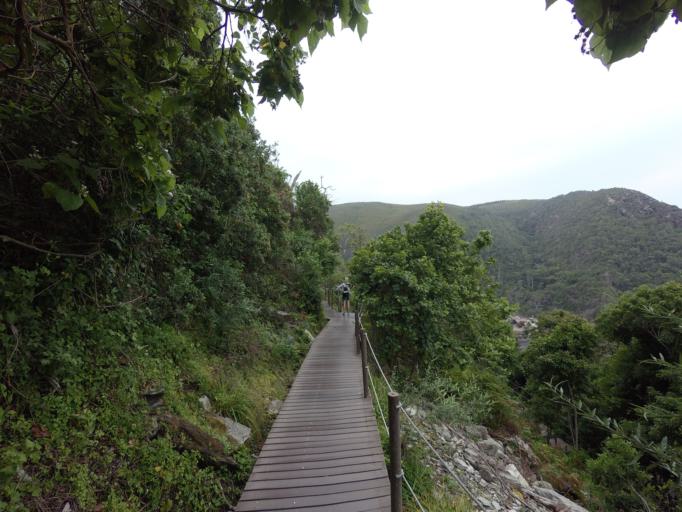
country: ZA
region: Eastern Cape
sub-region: Cacadu District Municipality
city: Kareedouw
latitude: -34.0198
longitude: 23.9017
